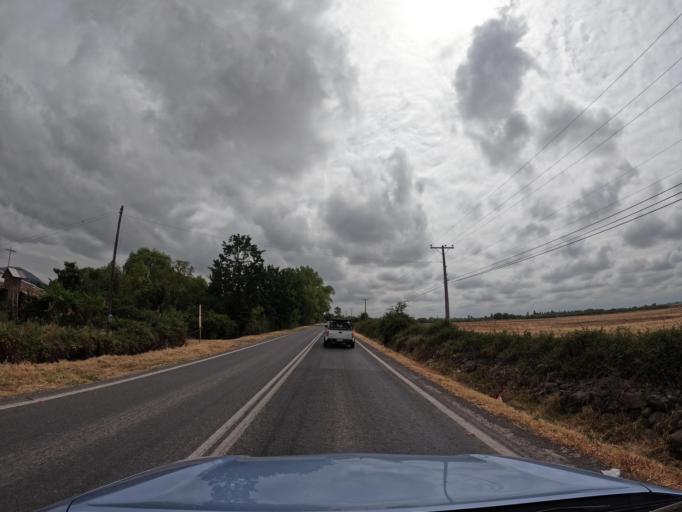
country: CL
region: Maule
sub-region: Provincia de Curico
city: Teno
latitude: -34.8479
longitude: -71.1897
